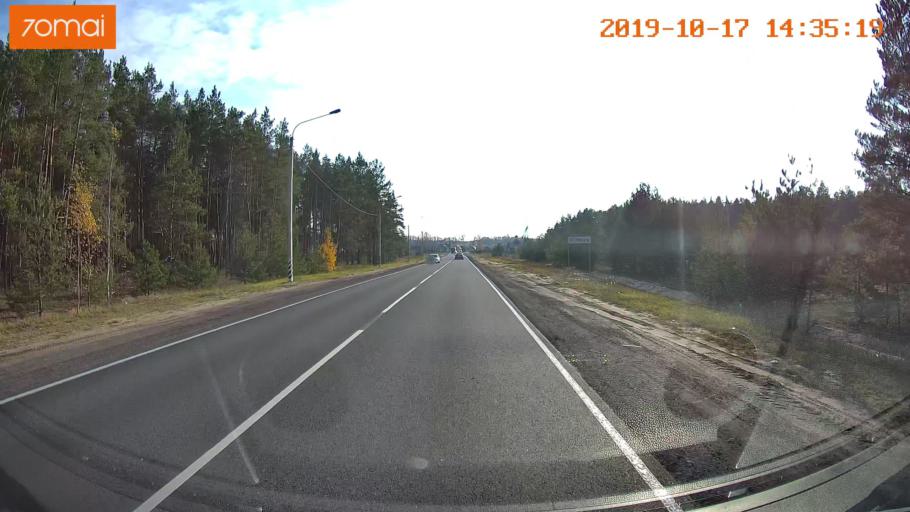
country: RU
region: Rjazan
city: Solotcha
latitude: 54.9013
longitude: 40.0028
